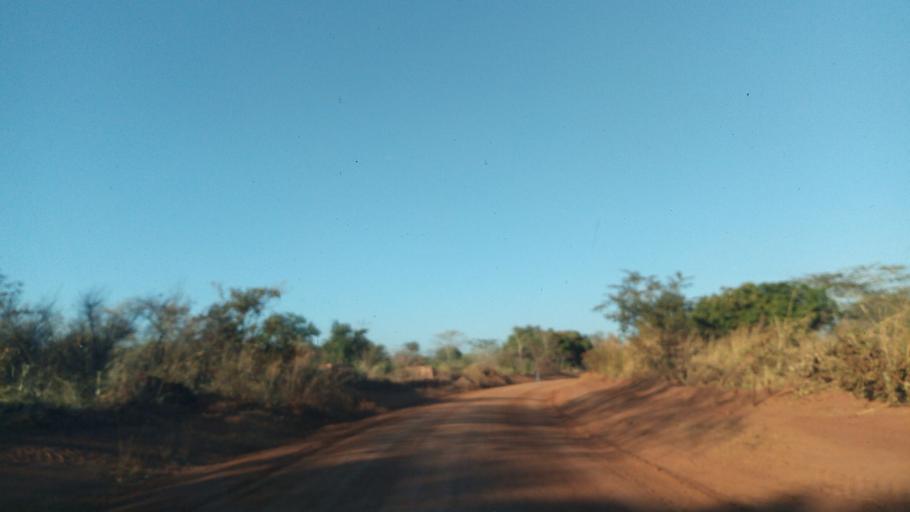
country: ZM
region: Luapula
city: Mwense
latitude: -10.4298
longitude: 28.5999
